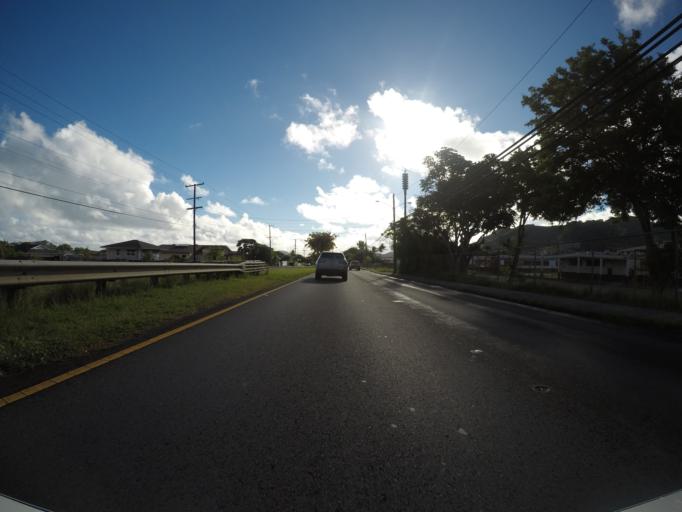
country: US
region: Hawaii
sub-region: Honolulu County
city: Kane'ohe
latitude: 21.4040
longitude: -157.7963
